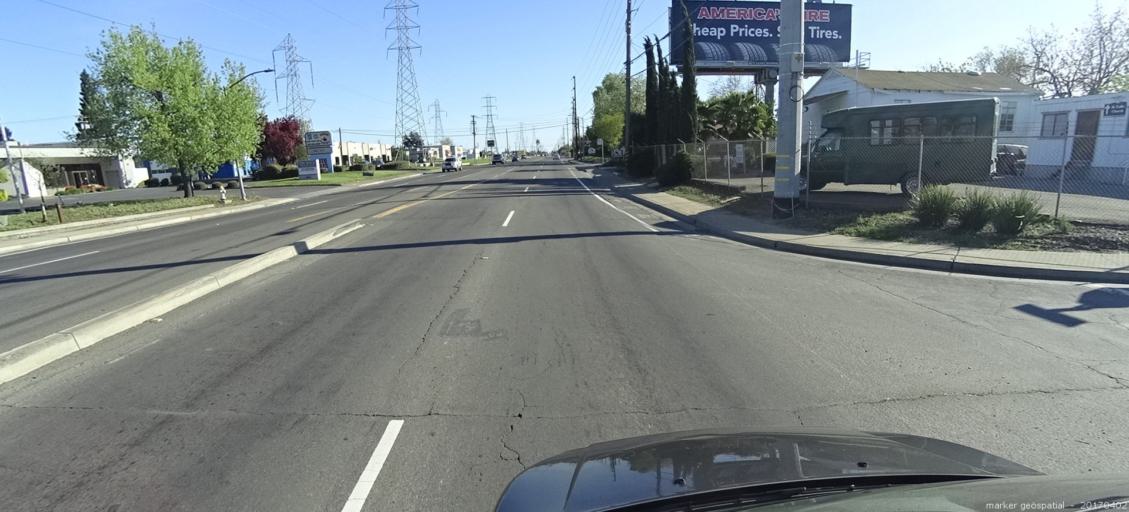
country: US
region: California
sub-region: Sacramento County
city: Florin
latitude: 38.5389
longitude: -121.4093
